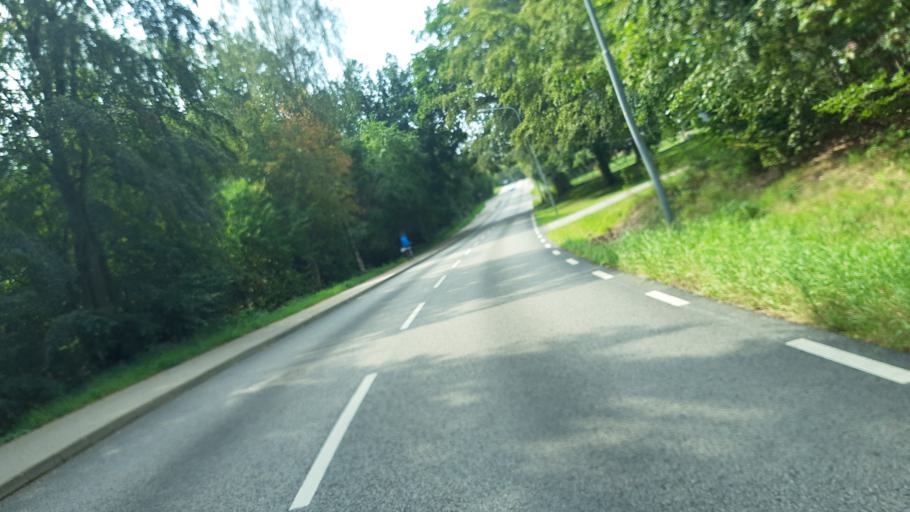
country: SE
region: Blekinge
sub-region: Ronneby Kommun
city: Ronneby
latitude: 56.1738
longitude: 15.2929
